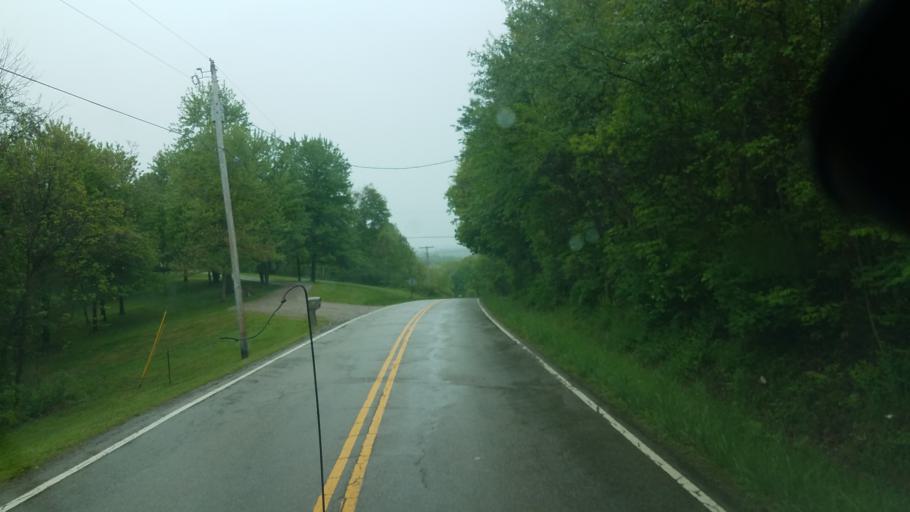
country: US
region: Ohio
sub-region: Muskingum County
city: Frazeysburg
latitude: 40.1003
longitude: -82.0983
